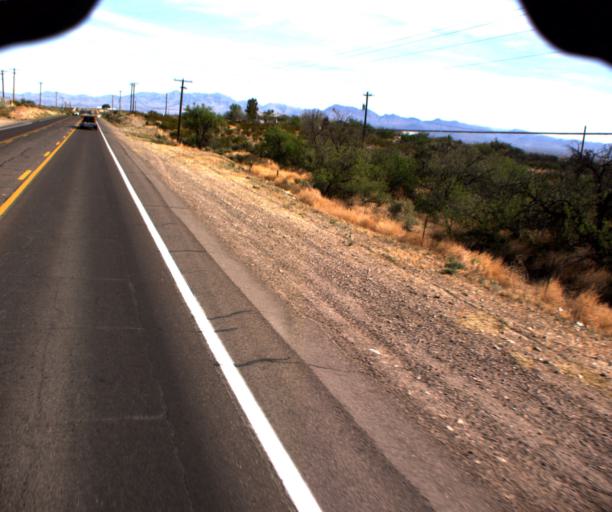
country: US
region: Arizona
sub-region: Graham County
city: Cactus Flat
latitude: 32.7734
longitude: -109.7162
